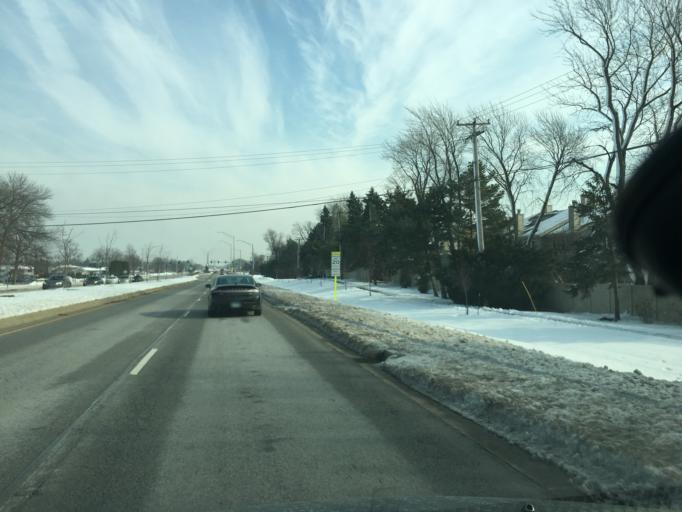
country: US
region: Illinois
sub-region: DuPage County
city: Darien
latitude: 41.7515
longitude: -87.9817
